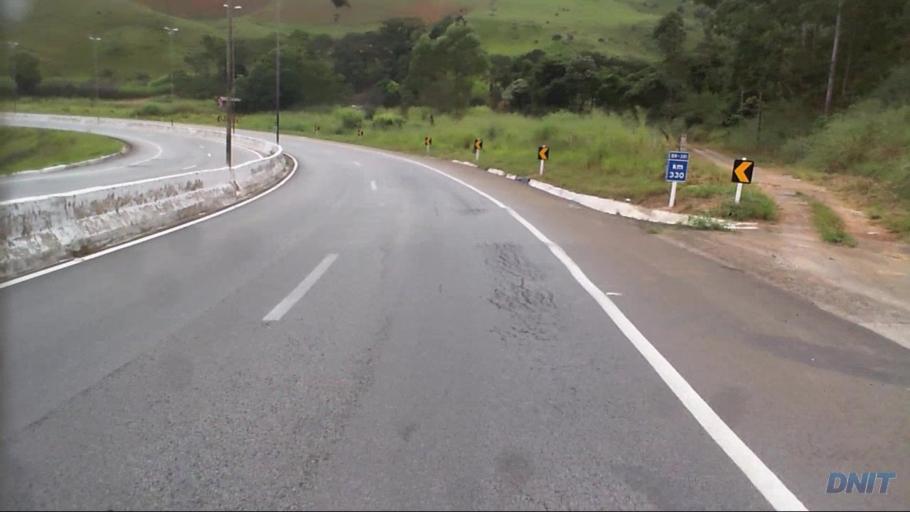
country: BR
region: Minas Gerais
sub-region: Nova Era
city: Nova Era
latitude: -19.7613
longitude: -43.0465
